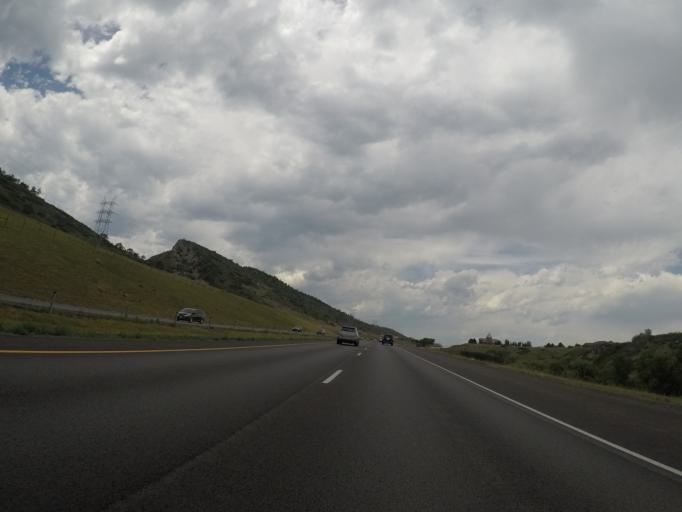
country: US
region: Colorado
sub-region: Jefferson County
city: Ken Caryl
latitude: 39.5986
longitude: -105.1515
